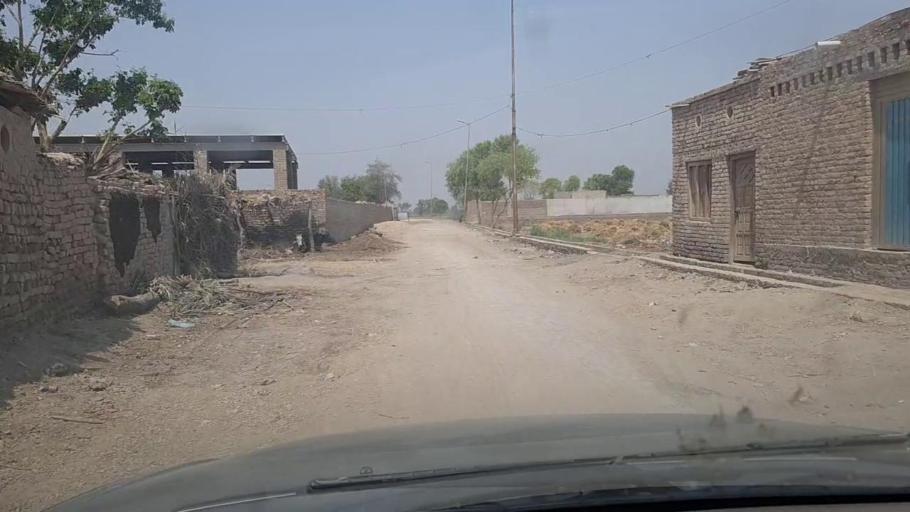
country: PK
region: Sindh
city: Adilpur
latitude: 27.9384
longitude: 69.3157
